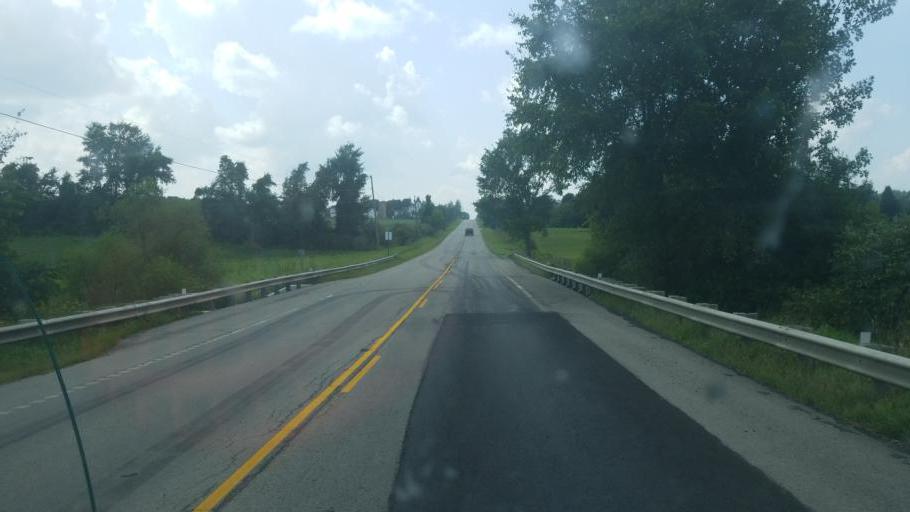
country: US
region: Ohio
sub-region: Huron County
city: New London
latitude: 41.0292
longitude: -82.4209
